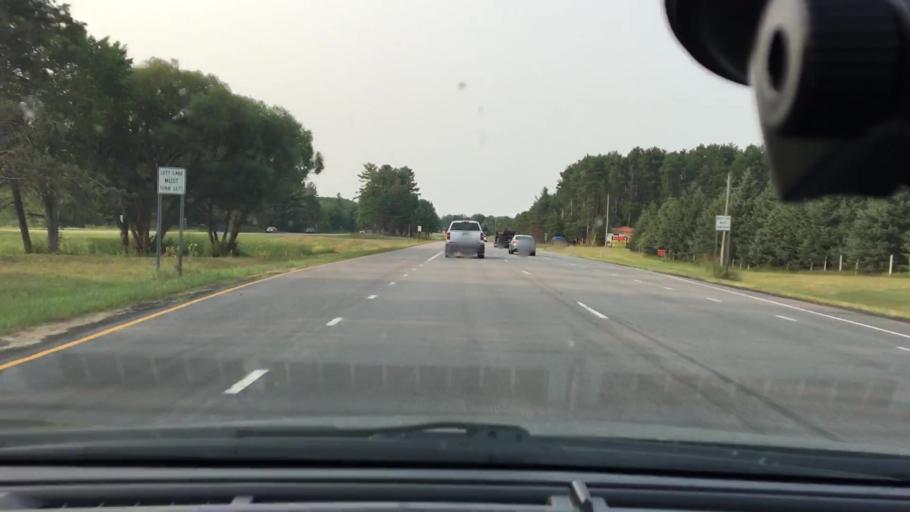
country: US
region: Minnesota
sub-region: Mille Lacs County
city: Princeton
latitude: 45.5258
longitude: -93.5826
